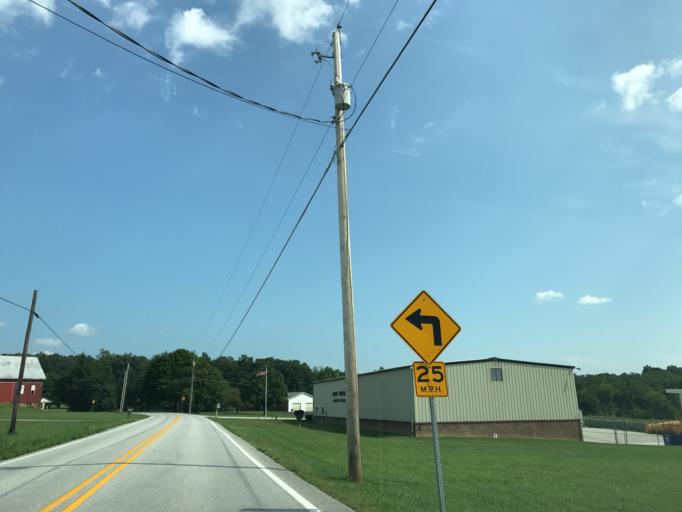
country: US
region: Pennsylvania
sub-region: Adams County
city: Mount Pleasant
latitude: 39.7521
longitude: -77.0313
